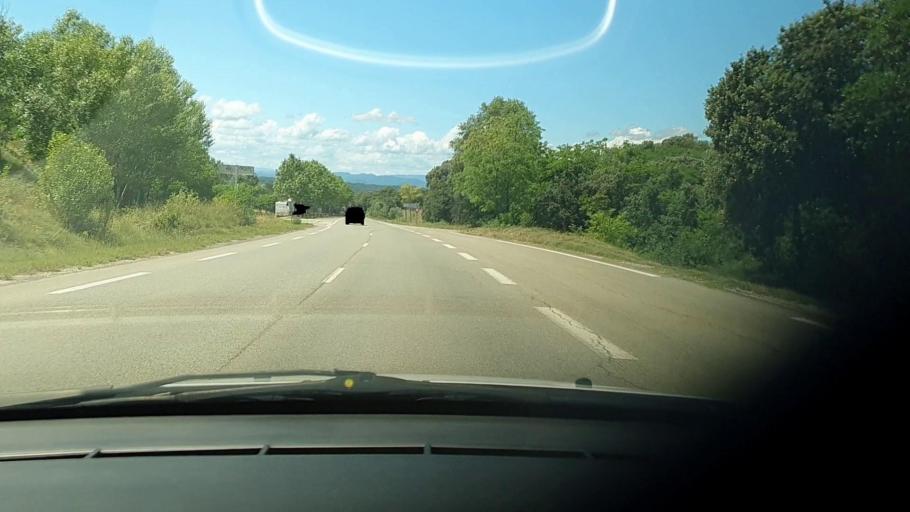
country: FR
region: Languedoc-Roussillon
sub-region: Departement du Gard
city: Moussac
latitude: 44.0640
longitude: 4.2549
